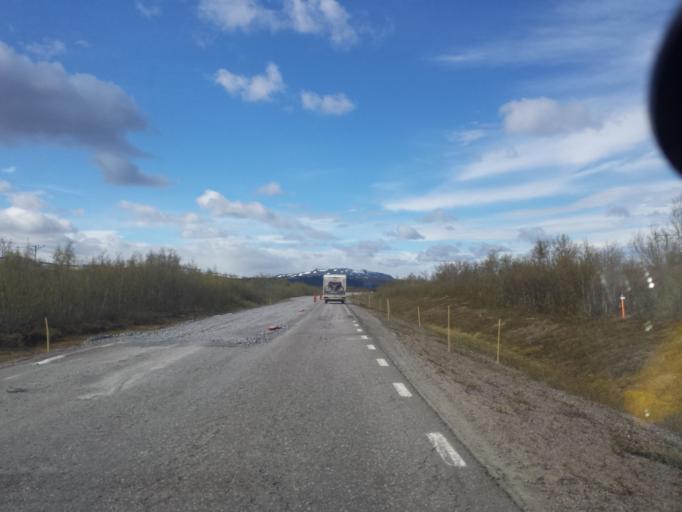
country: SE
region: Norrbotten
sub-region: Kiruna Kommun
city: Kiruna
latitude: 68.0058
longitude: 19.8506
